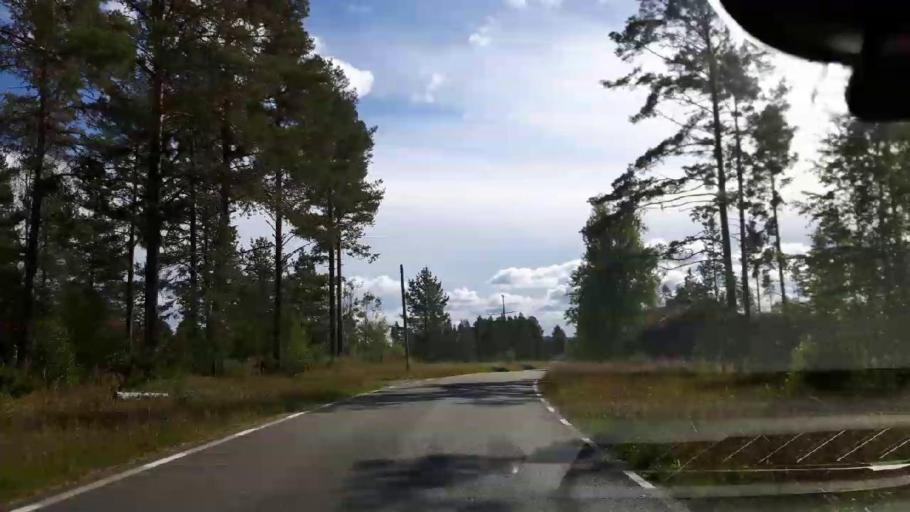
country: SE
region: Jaemtland
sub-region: Braecke Kommun
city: Braecke
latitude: 63.2159
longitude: 15.3384
